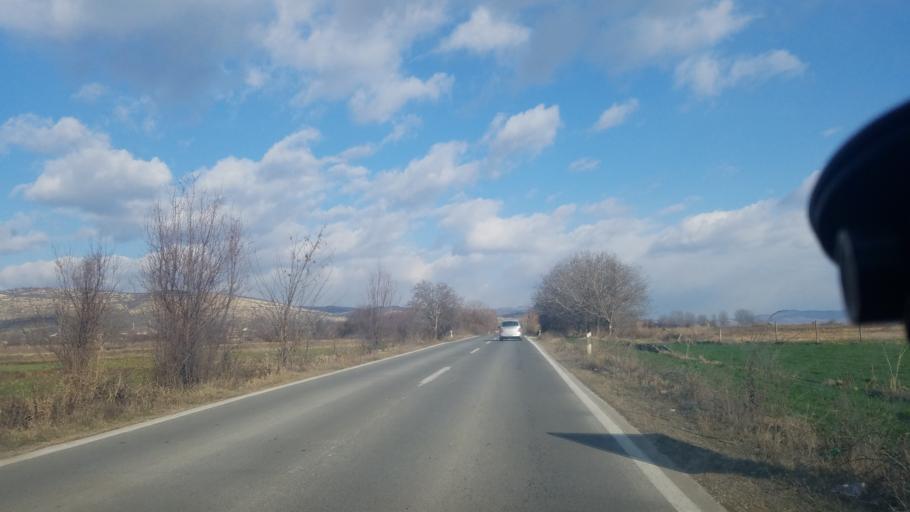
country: MK
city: Obleshevo
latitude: 41.8955
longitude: 22.3568
